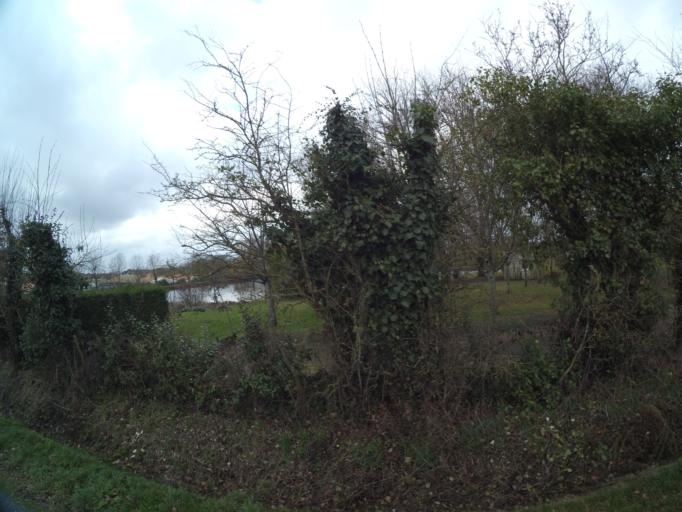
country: FR
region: Pays de la Loire
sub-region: Departement de la Vendee
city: Saint-Hilaire-de-Loulay
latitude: 47.0064
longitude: -1.3215
